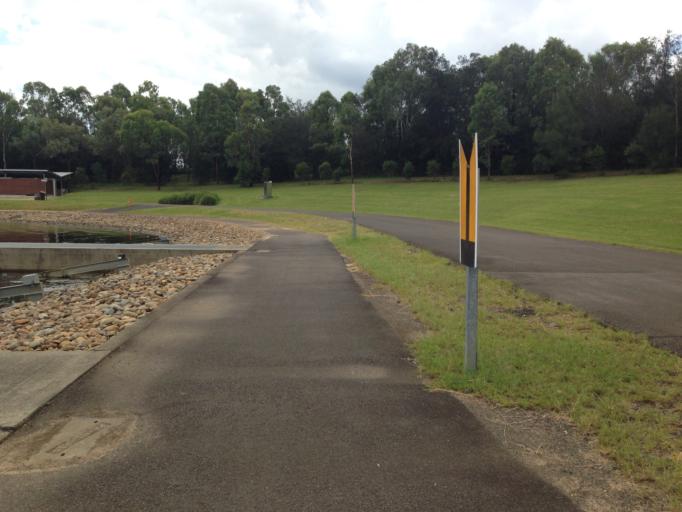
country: AU
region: New South Wales
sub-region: Penrith Municipality
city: Penrith
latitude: -33.7251
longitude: 150.6928
